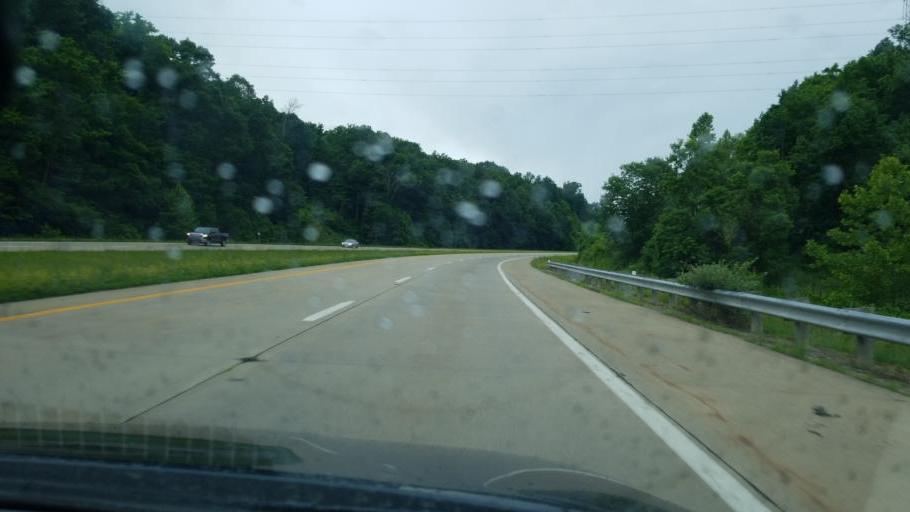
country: US
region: West Virginia
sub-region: Wood County
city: Washington
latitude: 39.2159
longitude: -81.8569
